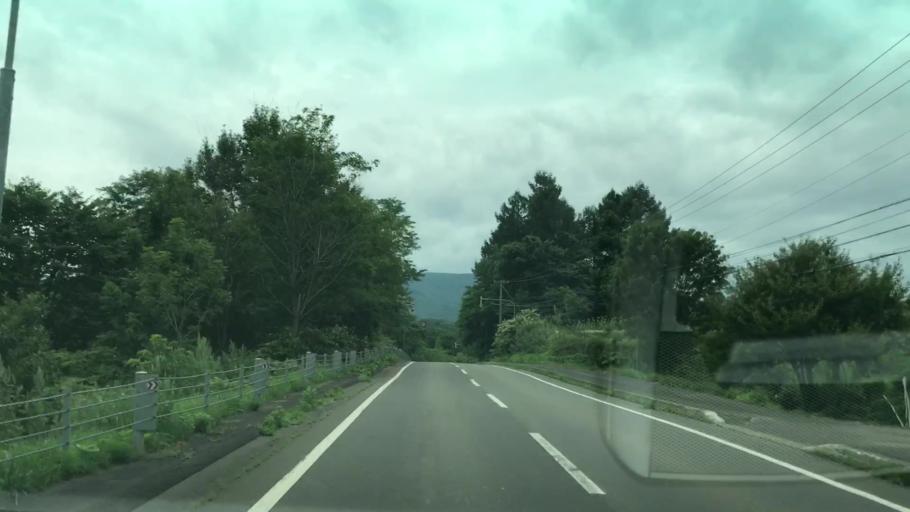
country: JP
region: Hokkaido
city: Yoichi
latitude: 43.0671
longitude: 140.8198
